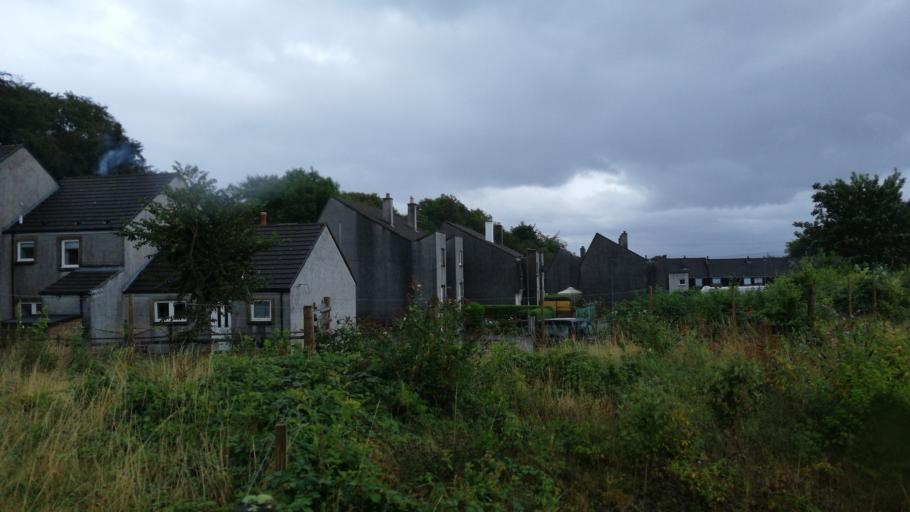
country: GB
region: Scotland
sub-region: Argyll and Bute
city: Isle Of Mull
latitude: 56.4789
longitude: -5.7155
